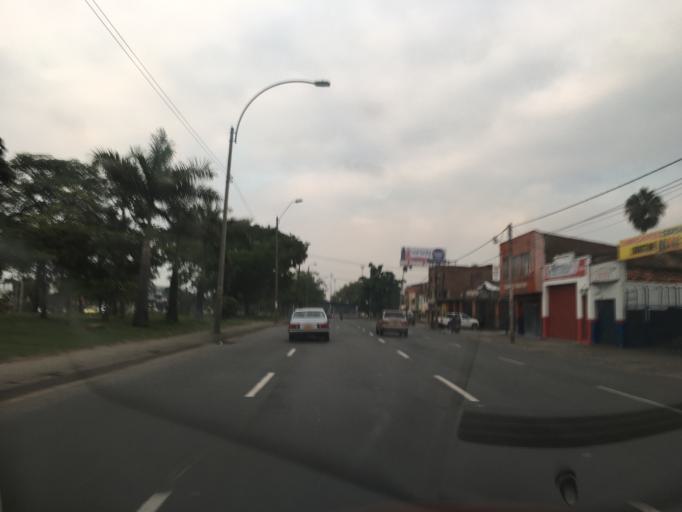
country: CO
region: Valle del Cauca
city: Cali
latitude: 3.4484
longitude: -76.5182
